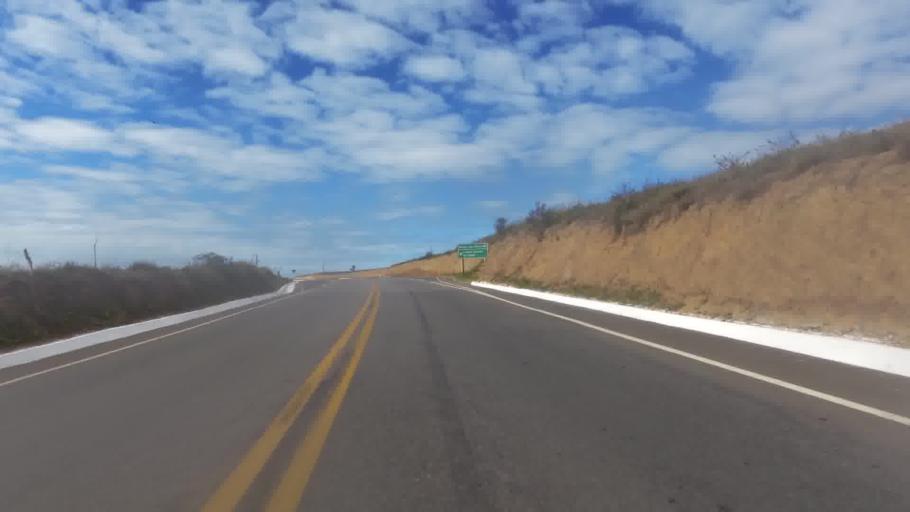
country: BR
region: Espirito Santo
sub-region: Marataizes
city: Marataizes
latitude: -21.0874
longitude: -40.8501
